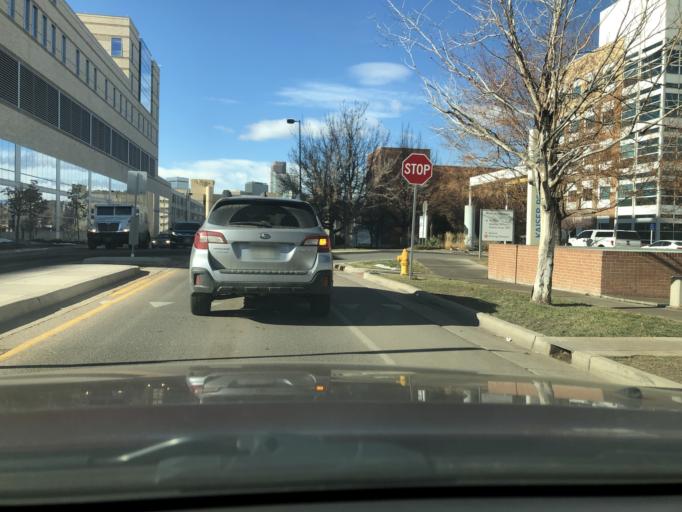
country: US
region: Colorado
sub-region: Denver County
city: Denver
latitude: 39.7470
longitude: -104.9705
